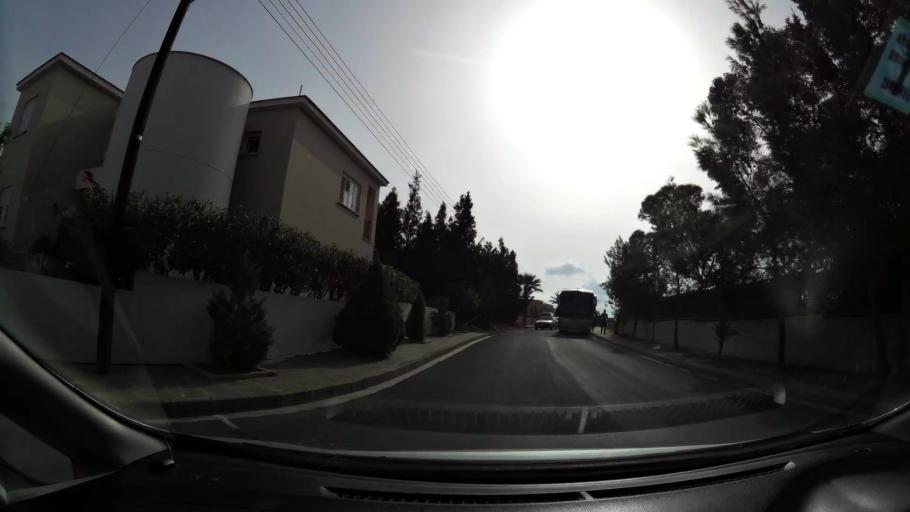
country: CY
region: Lefkosia
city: Geri
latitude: 35.0760
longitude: 33.3883
